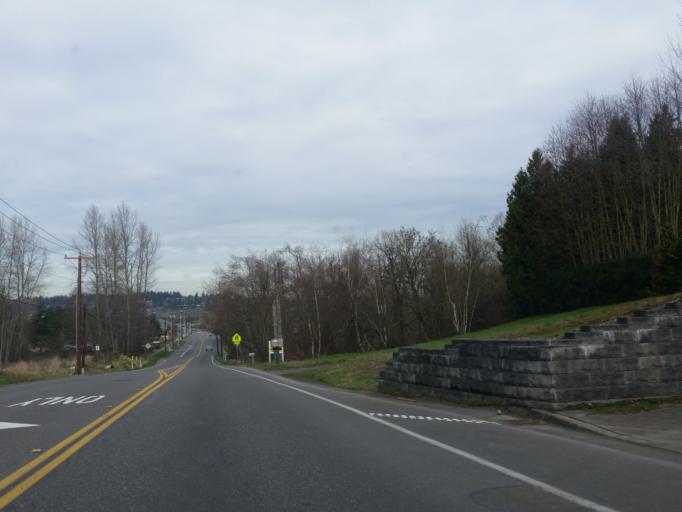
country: US
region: Washington
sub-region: Pierce County
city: Sumner
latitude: 47.1794
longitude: -122.2561
